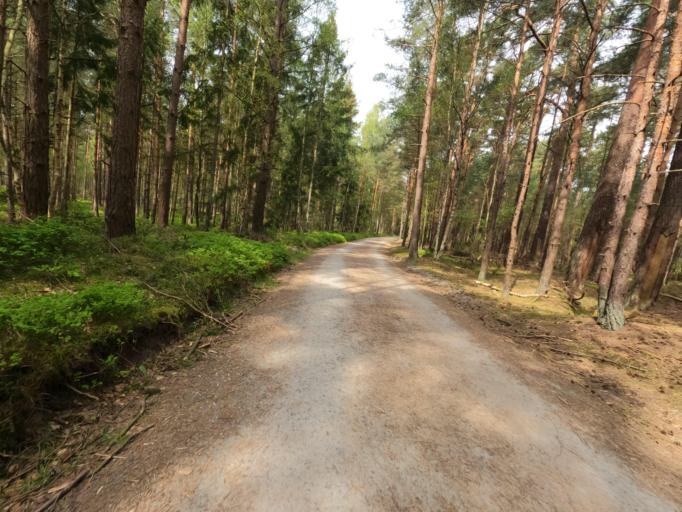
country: DE
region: Mecklenburg-Vorpommern
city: Ostseebad Prerow
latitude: 54.4512
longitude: 12.5197
